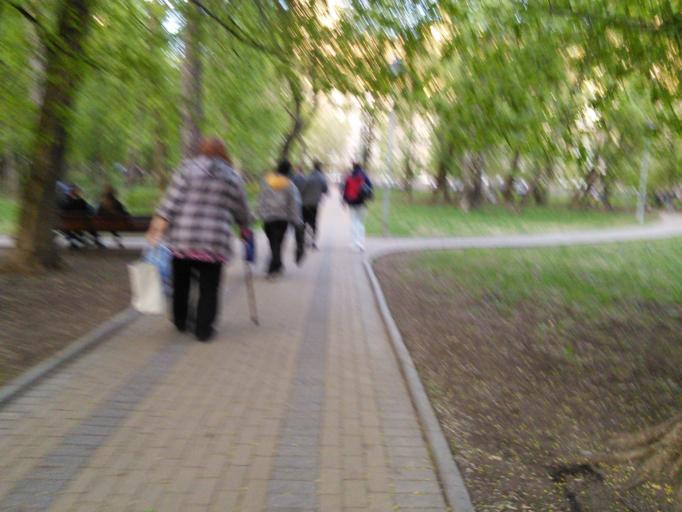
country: RU
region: Moscow
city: Pokrovskoye-Streshnevo
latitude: 55.8285
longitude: 37.4540
